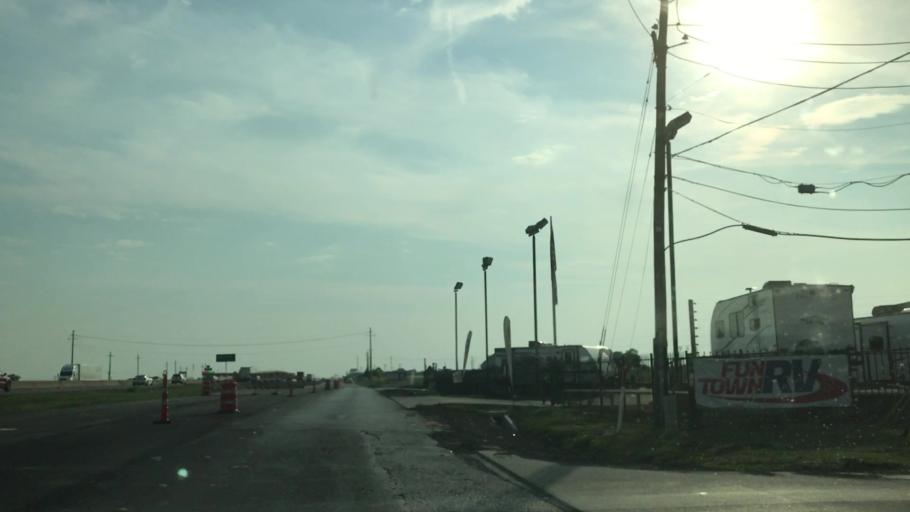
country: US
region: Texas
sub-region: Rockwall County
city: Fate
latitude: 32.9215
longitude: -96.4118
